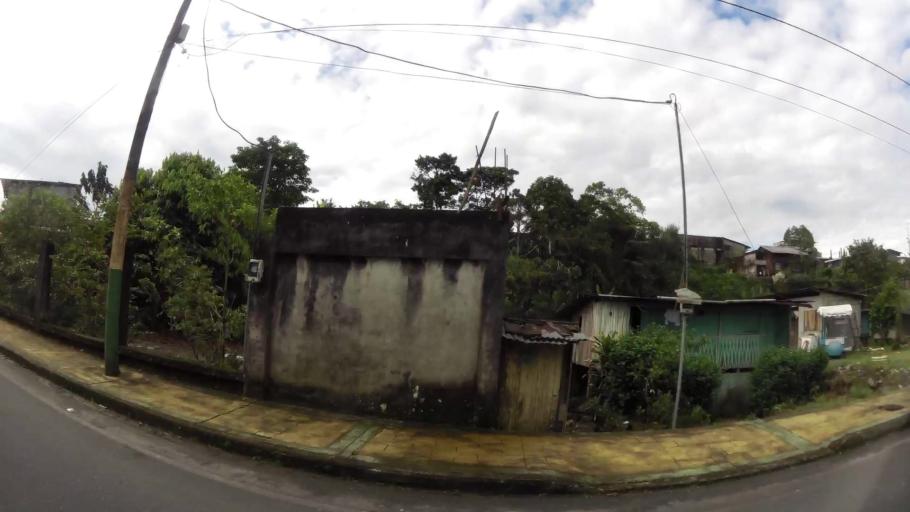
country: EC
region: Pastaza
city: Puyo
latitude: -1.4850
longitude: -77.9942
